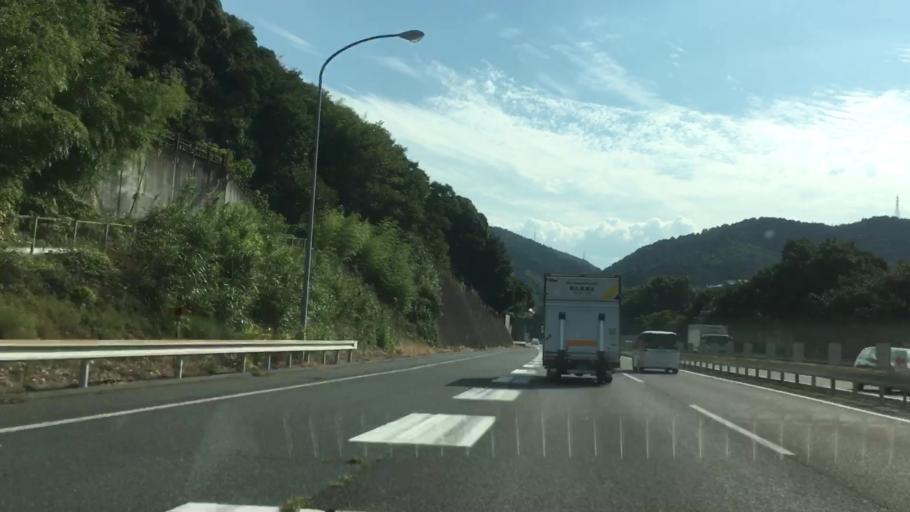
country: JP
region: Yamaguchi
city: Otake
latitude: 34.2415
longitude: 132.2155
